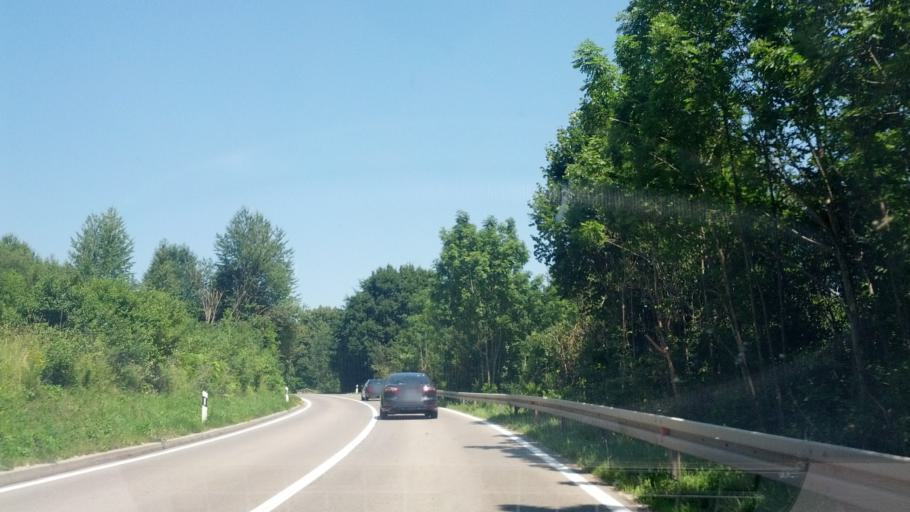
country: BA
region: Federation of Bosnia and Herzegovina
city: Izacic
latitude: 44.8859
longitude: 15.7273
